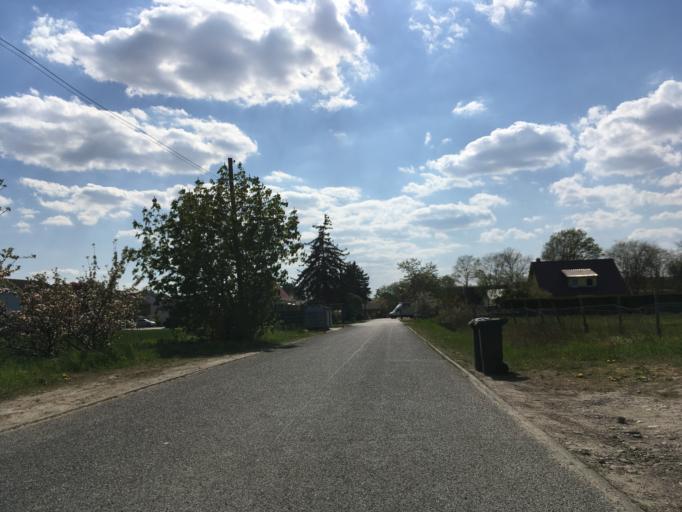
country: DE
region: Brandenburg
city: Ahrensfelde
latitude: 52.6081
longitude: 13.6061
